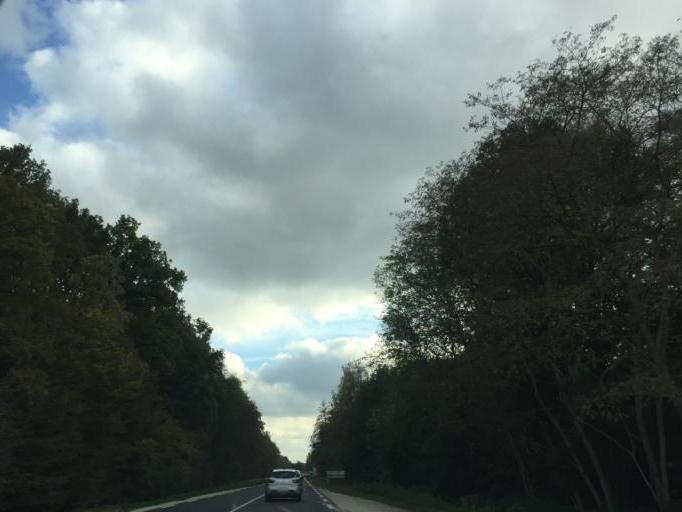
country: FR
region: Ile-de-France
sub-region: Departement de Seine-et-Marne
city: Villeneuve-le-Comte
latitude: 48.8190
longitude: 2.8419
